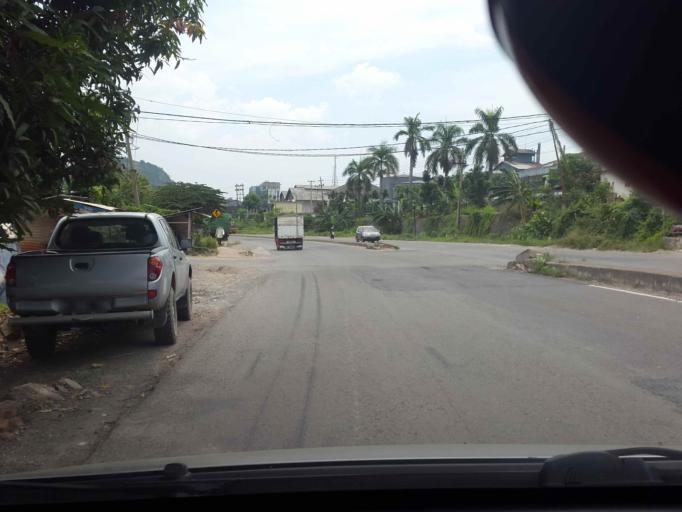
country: ID
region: Lampung
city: Panjang
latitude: -5.4363
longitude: 105.3011
